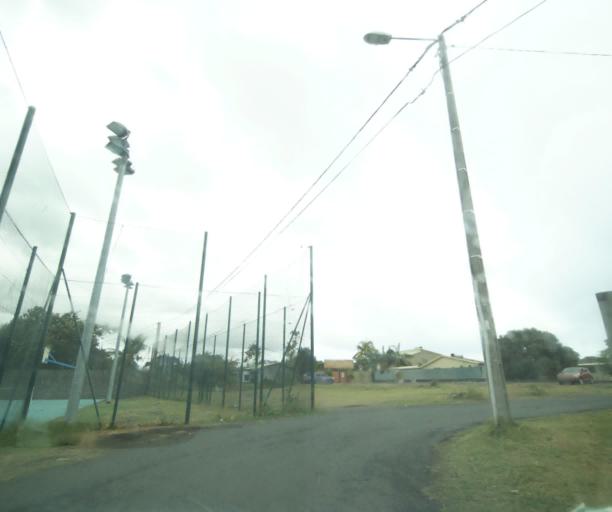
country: RE
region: Reunion
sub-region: Reunion
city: Saint-Paul
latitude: -20.9931
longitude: 55.2860
